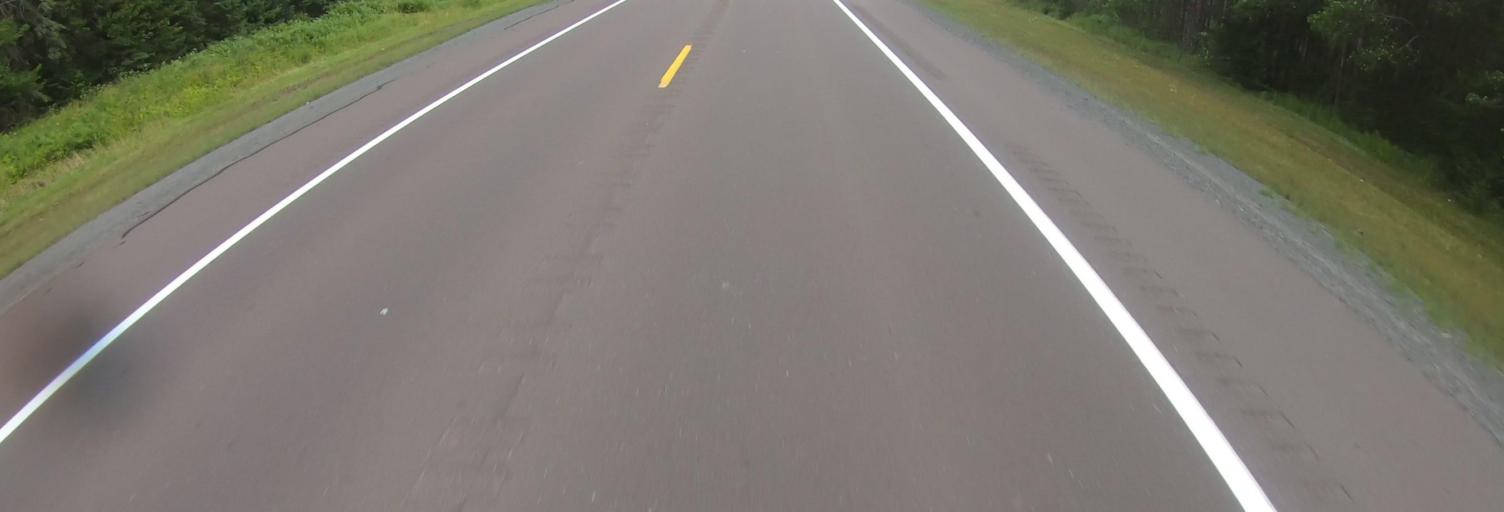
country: US
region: Michigan
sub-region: Baraga County
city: Baraga
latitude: 46.9189
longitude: -88.4639
